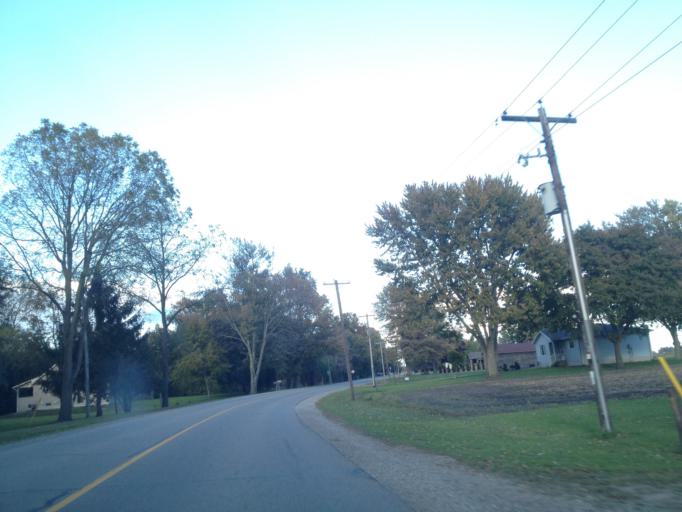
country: CA
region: Ontario
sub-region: Lambton County
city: Walpole Island
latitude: 42.3165
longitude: -82.4193
